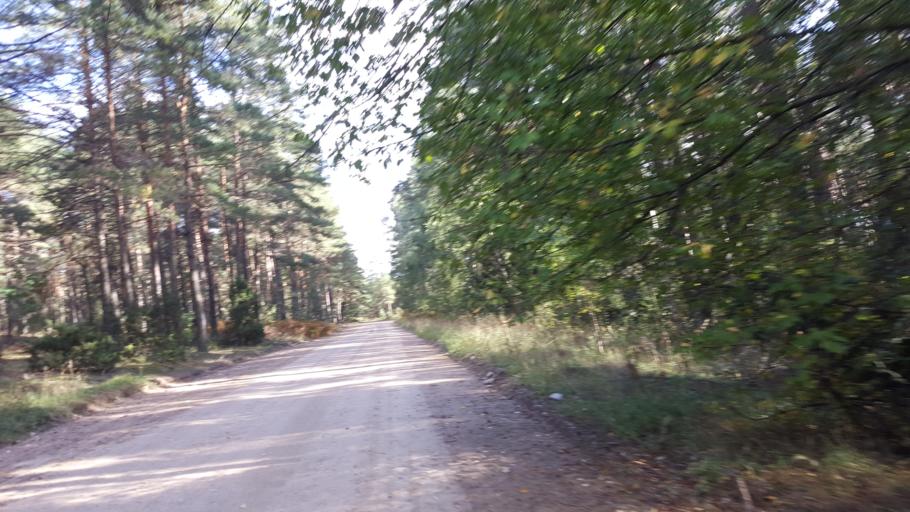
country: BY
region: Brest
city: Kamyanyets
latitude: 52.4355
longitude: 23.9425
